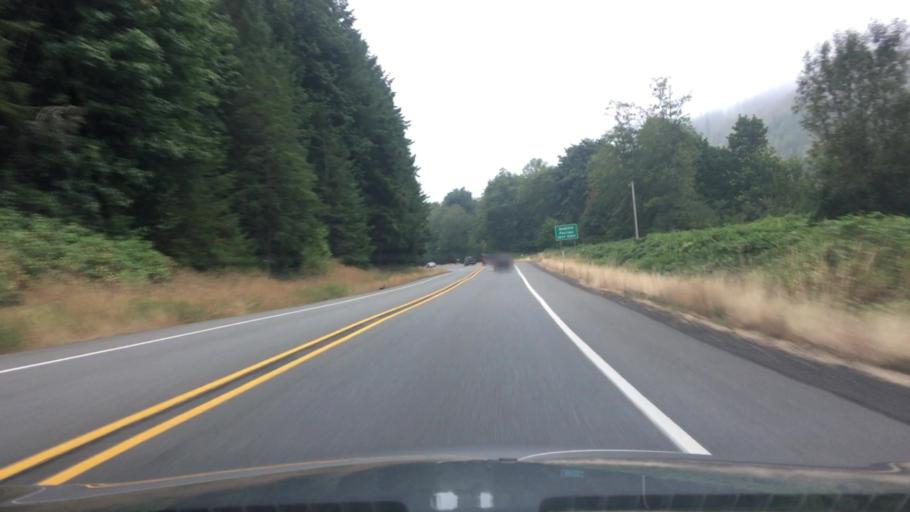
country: US
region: Washington
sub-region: Jefferson County
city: Port Hadlock-Irondale
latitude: 47.9629
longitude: -122.8814
